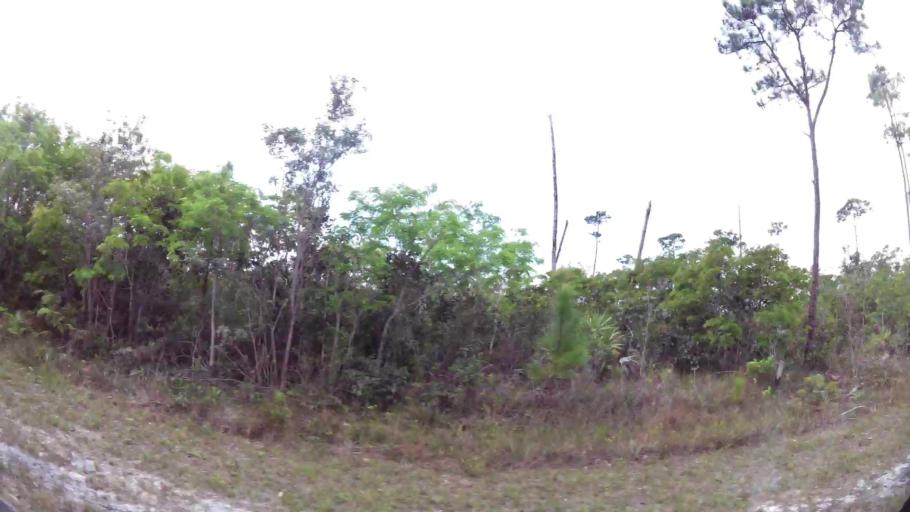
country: BS
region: Freeport
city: Lucaya
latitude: 26.5518
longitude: -78.5743
